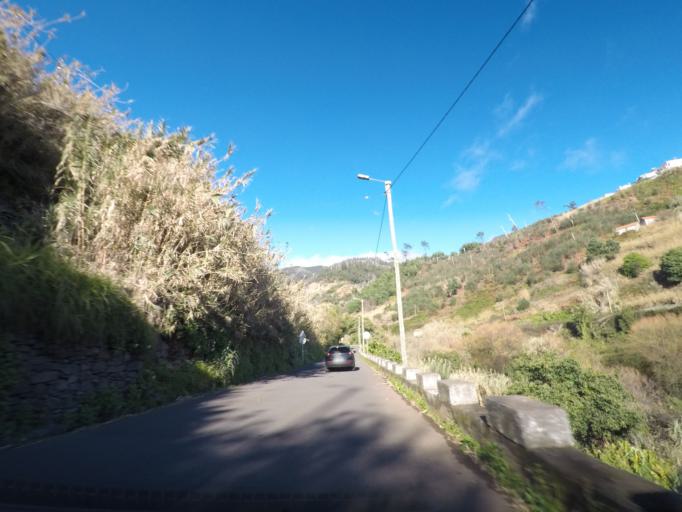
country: PT
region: Madeira
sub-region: Calheta
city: Arco da Calheta
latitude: 32.7311
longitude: -17.1536
